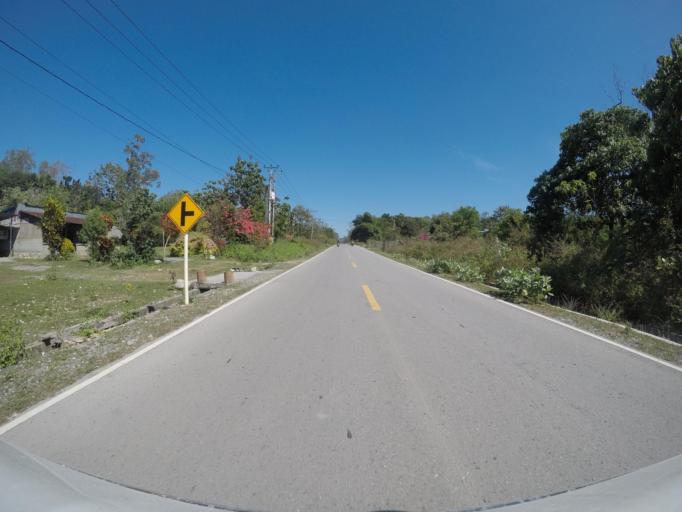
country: TL
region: Viqueque
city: Viqueque
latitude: -8.9744
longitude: 126.0377
